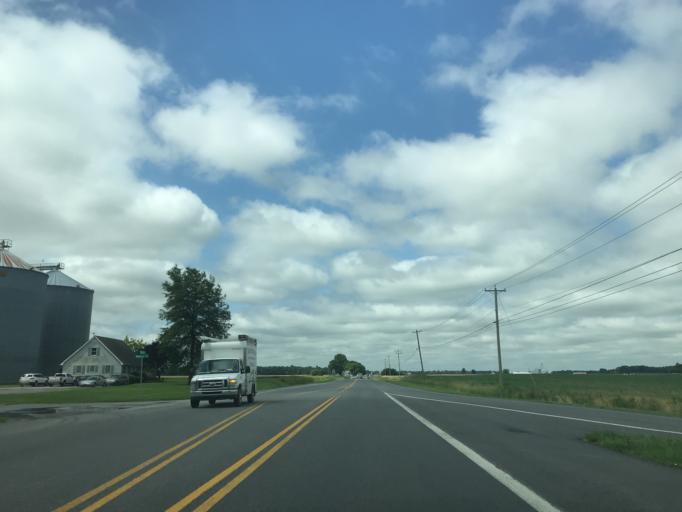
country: US
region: Maryland
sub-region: Caroline County
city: Ridgely
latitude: 38.9385
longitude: -75.8889
